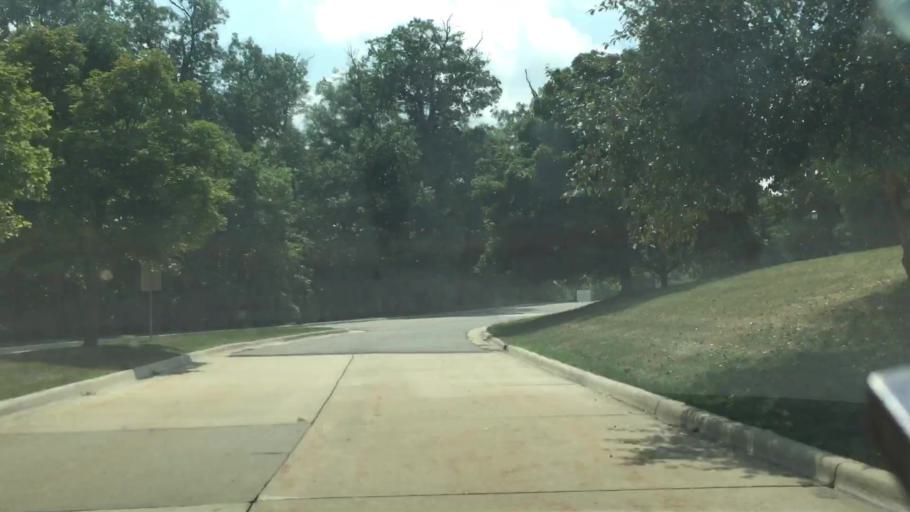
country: US
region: Michigan
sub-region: Oakland County
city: Auburn Hills
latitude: 42.6715
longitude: -83.2238
